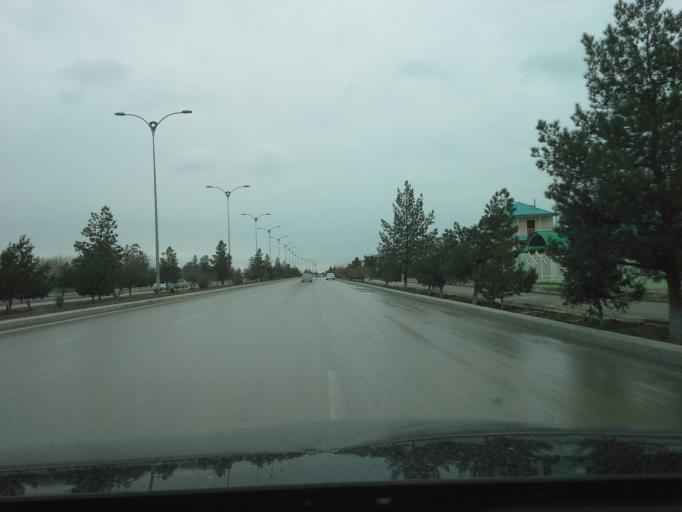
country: TM
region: Ahal
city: Abadan
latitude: 37.9644
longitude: 58.2223
